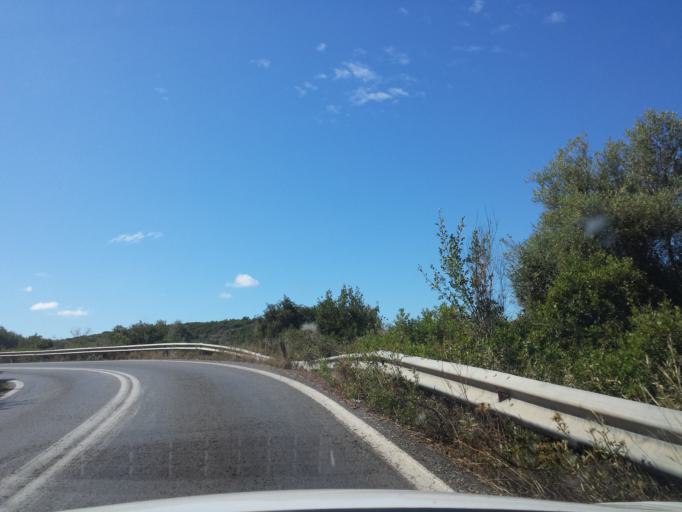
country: GR
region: Peloponnese
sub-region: Nomos Messinias
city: Pylos
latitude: 36.9409
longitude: 21.7462
